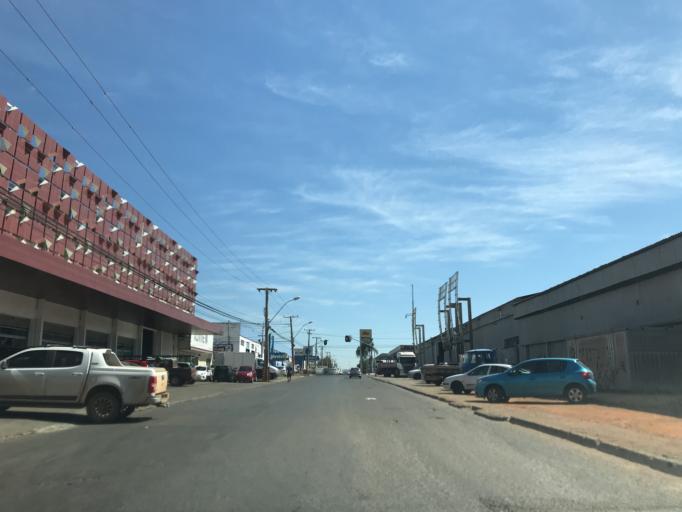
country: BR
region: Federal District
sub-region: Brasilia
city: Brasilia
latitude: -15.8103
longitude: -48.0730
